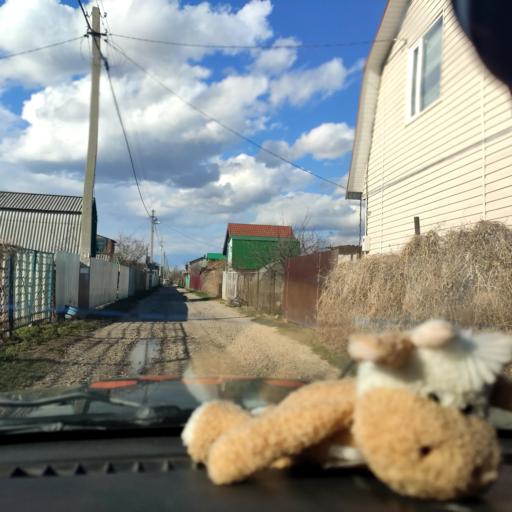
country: RU
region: Samara
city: Tol'yatti
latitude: 53.5935
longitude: 49.3076
